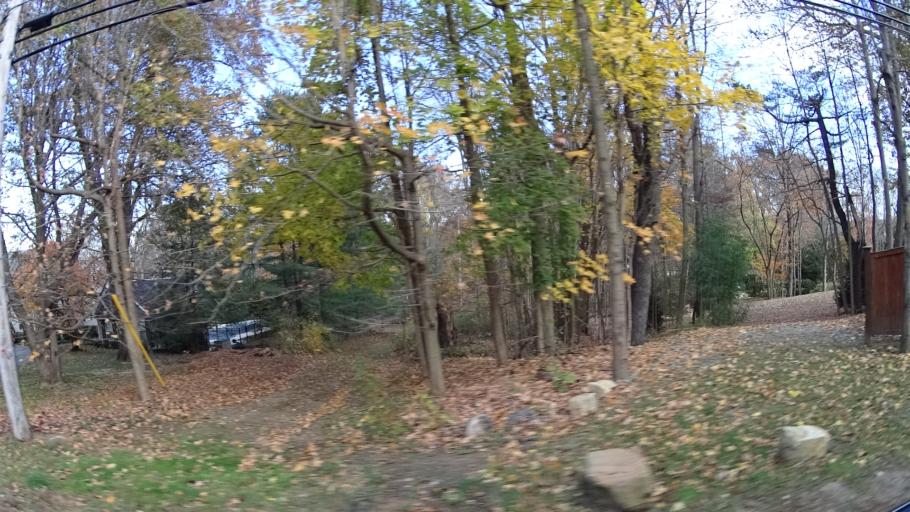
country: US
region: New Jersey
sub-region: Morris County
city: Madison
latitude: 40.7548
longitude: -74.4528
